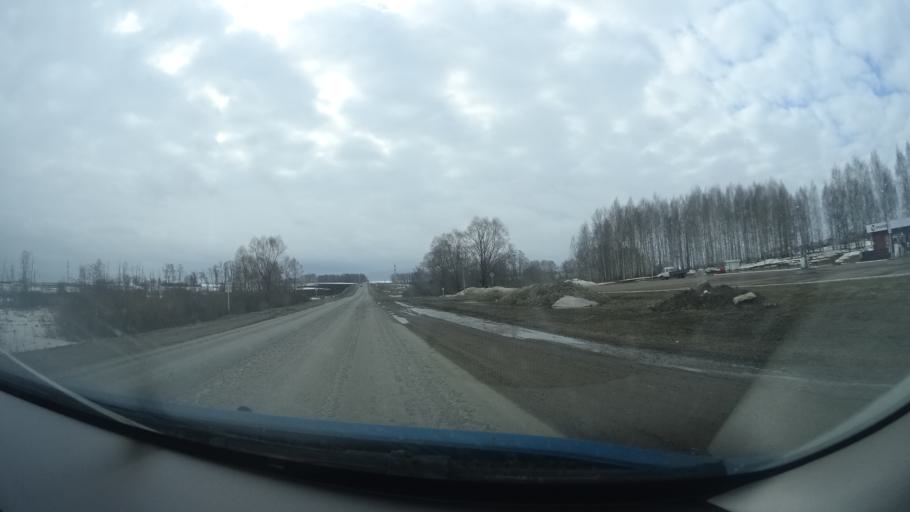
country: RU
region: Bashkortostan
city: Birsk
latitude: 55.4128
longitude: 55.5858
